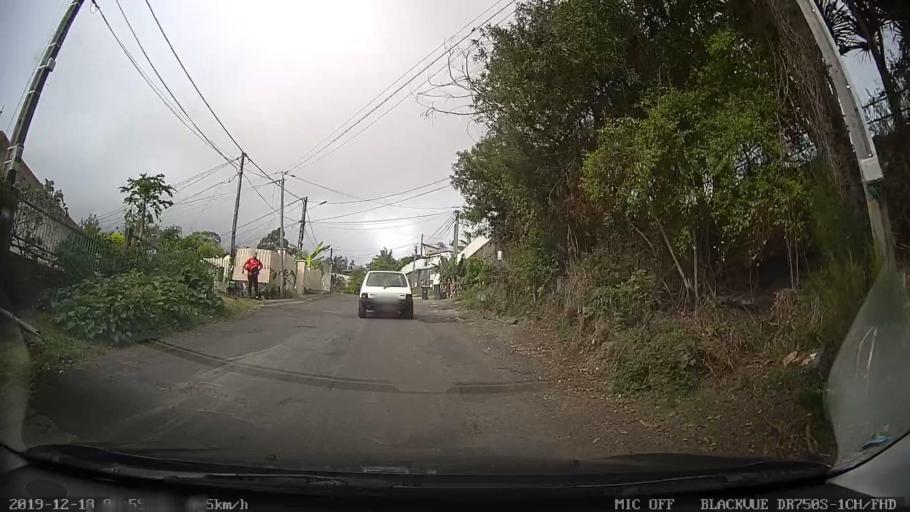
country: RE
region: Reunion
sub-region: Reunion
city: Le Tampon
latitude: -21.2546
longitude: 55.5170
